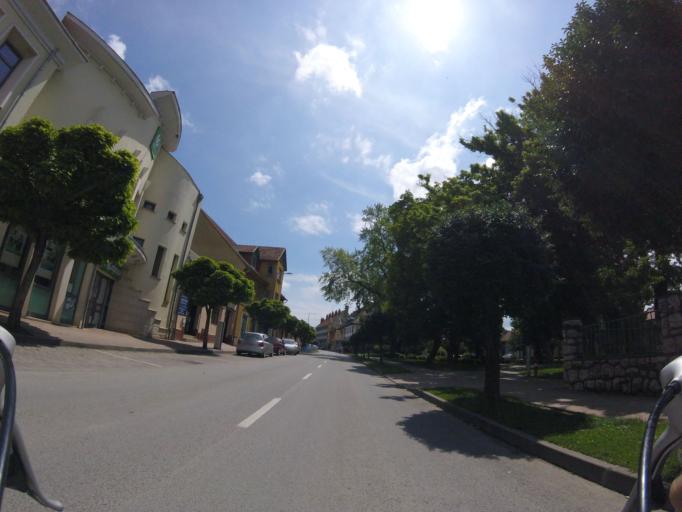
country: HU
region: Baranya
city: Siklos
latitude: 45.8561
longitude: 18.2954
